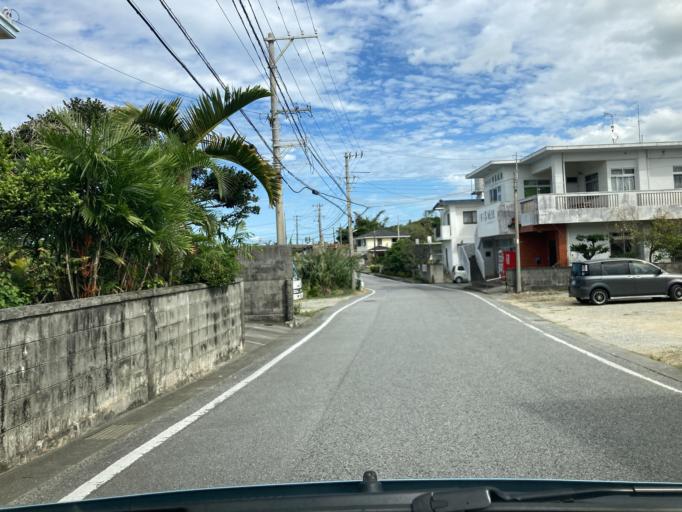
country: JP
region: Okinawa
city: Ishikawa
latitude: 26.4307
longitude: 127.7777
